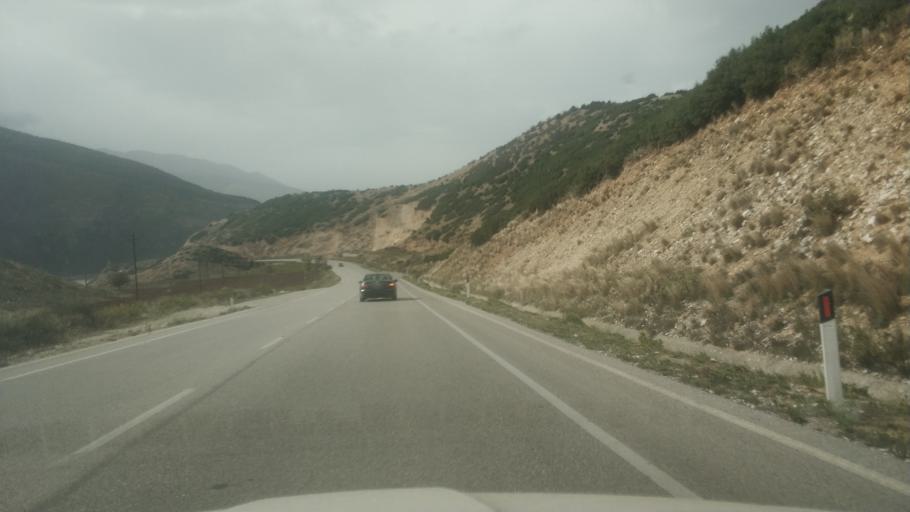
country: AL
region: Gjirokaster
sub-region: Rrethi i Tepelenes
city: Memaliaj
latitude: 40.3649
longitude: 19.9187
